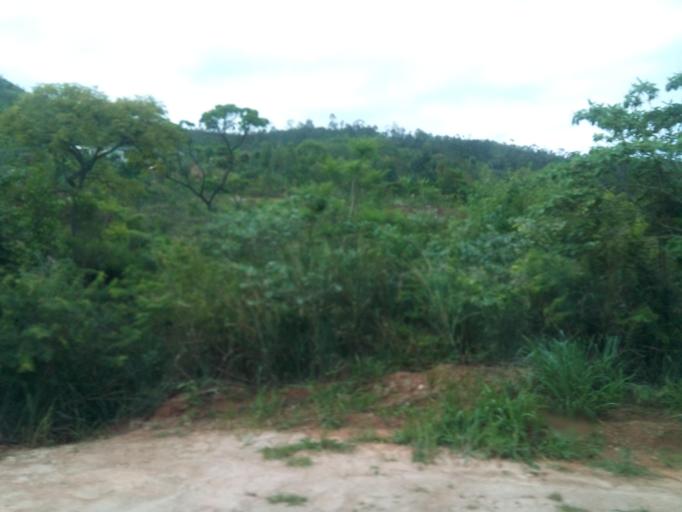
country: BR
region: Minas Gerais
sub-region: Caete
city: Caete
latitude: -19.9154
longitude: -43.7015
